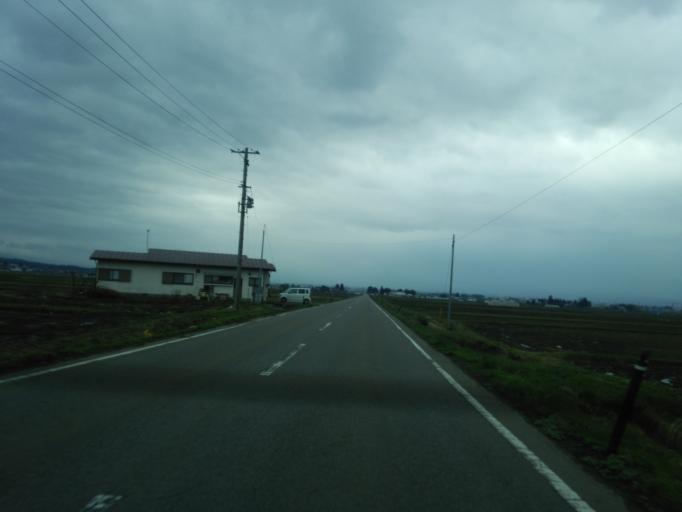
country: JP
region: Fukushima
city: Kitakata
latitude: 37.6411
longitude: 139.9179
